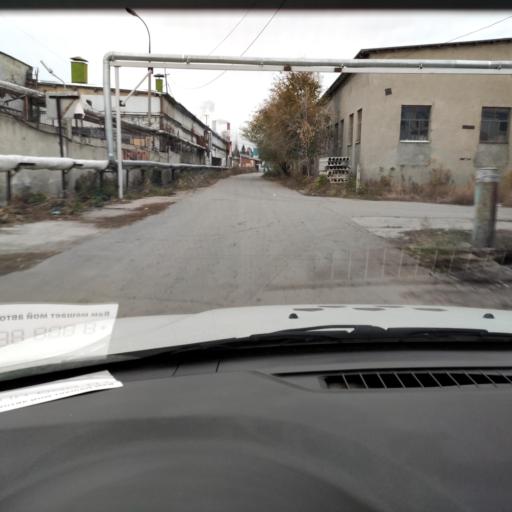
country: RU
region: Samara
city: Tol'yatti
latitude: 53.5315
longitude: 49.4482
